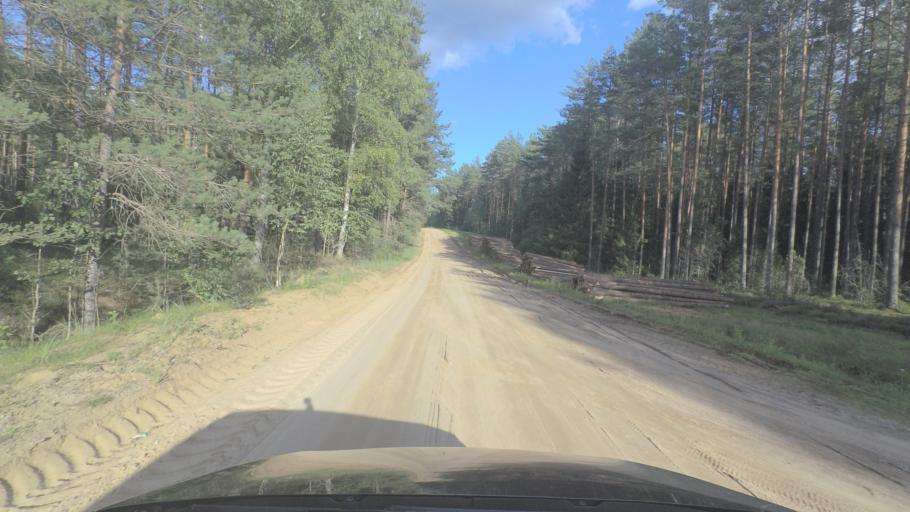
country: LT
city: Pabrade
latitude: 55.1537
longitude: 25.7816
